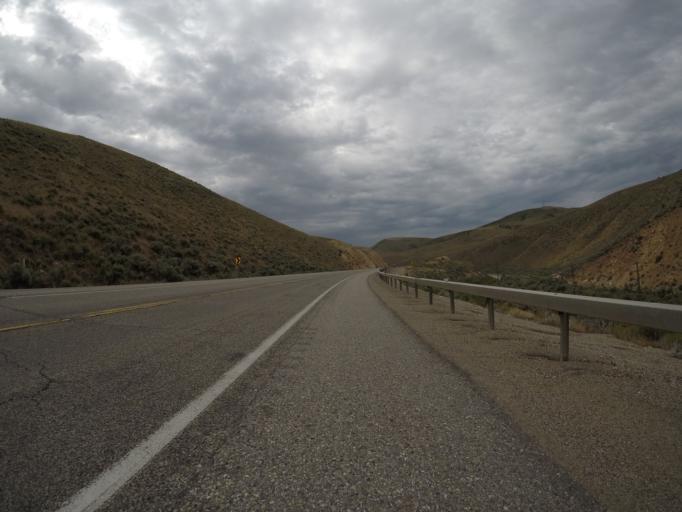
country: US
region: Wyoming
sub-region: Lincoln County
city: Kemmerer
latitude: 41.8239
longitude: -110.8087
